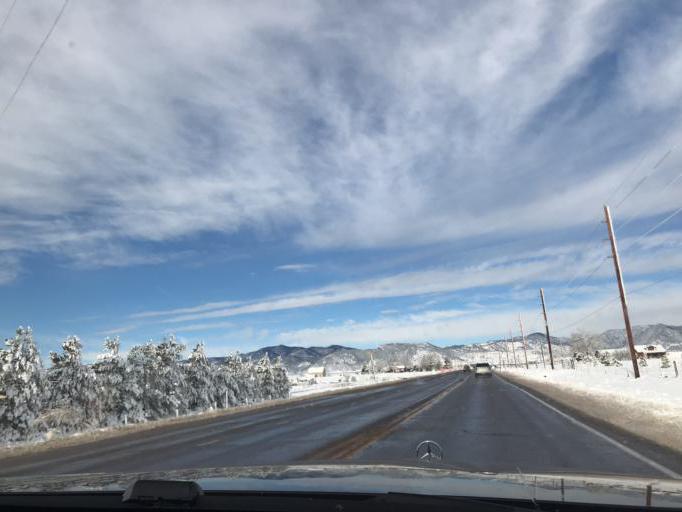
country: US
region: Colorado
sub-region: Jefferson County
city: Applewood
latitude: 39.8508
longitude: -105.1684
